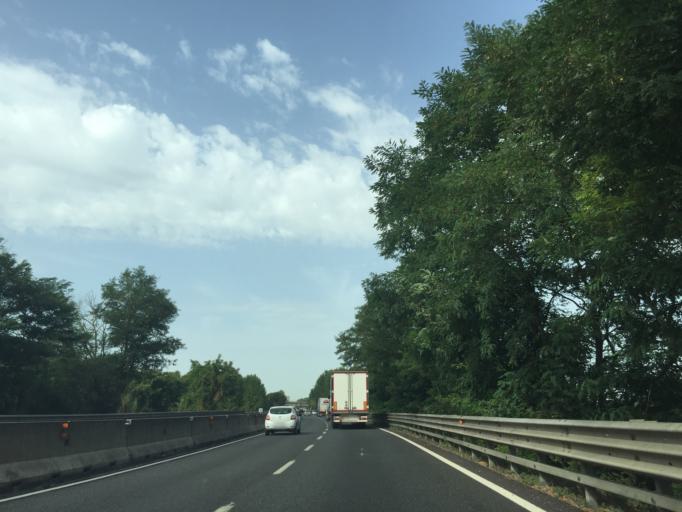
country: IT
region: Tuscany
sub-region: Province of Pisa
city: Montopoli
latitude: 43.6827
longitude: 10.7575
